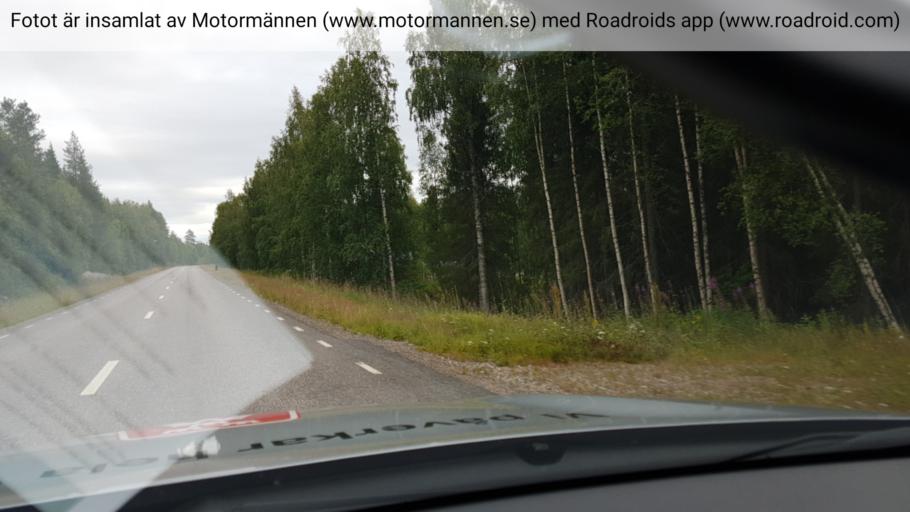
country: SE
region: Norrbotten
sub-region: Overkalix Kommun
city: OEverkalix
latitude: 66.4976
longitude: 22.7720
